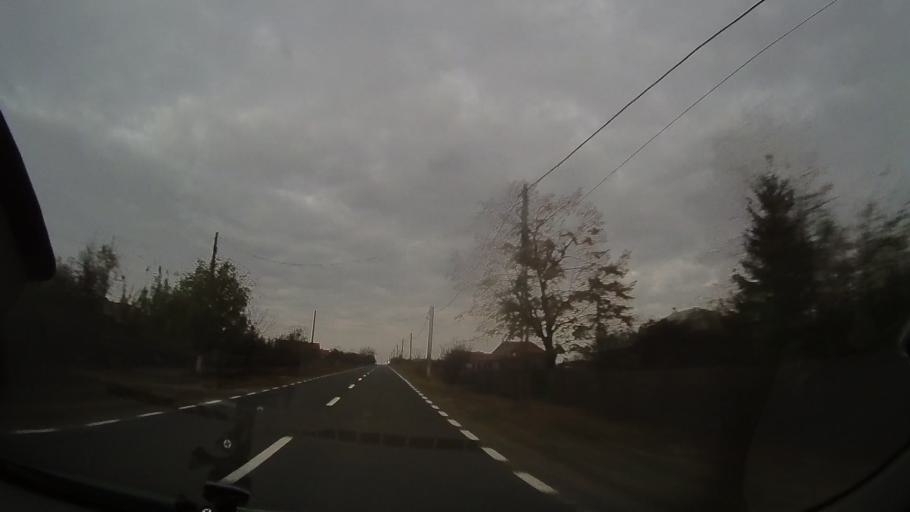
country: RO
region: Tulcea
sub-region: Comuna Nalbant
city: Nicolae Balcescu
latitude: 44.9992
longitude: 28.5914
